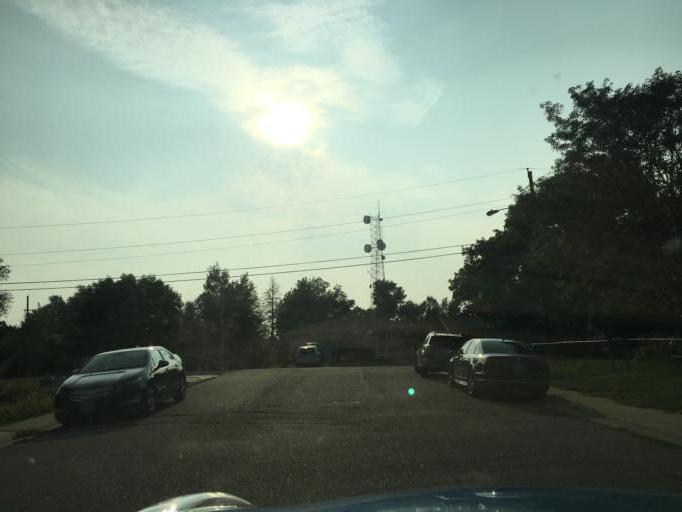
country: US
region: Colorado
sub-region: Arapahoe County
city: Glendale
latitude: 39.6917
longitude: -104.9343
